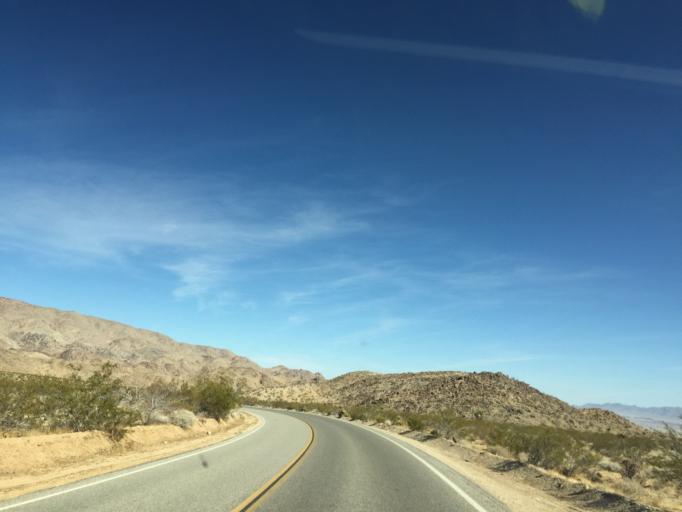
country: US
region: California
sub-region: San Bernardino County
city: Twentynine Palms
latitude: 34.0385
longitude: -116.0223
